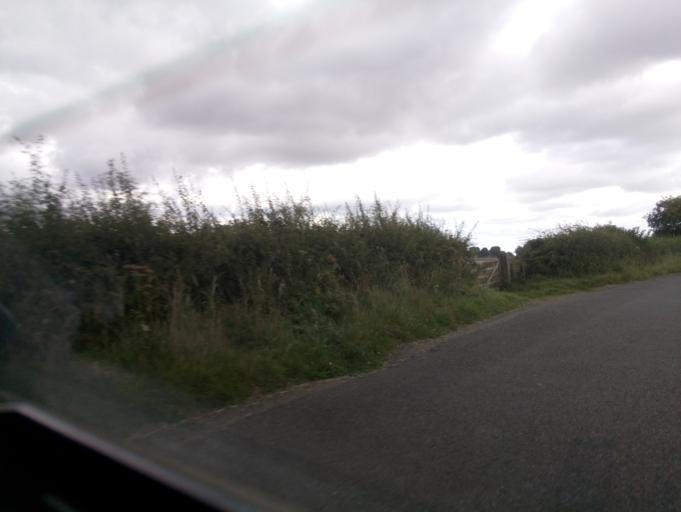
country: GB
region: England
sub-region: Gloucestershire
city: Chalford
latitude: 51.7791
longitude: -2.1022
